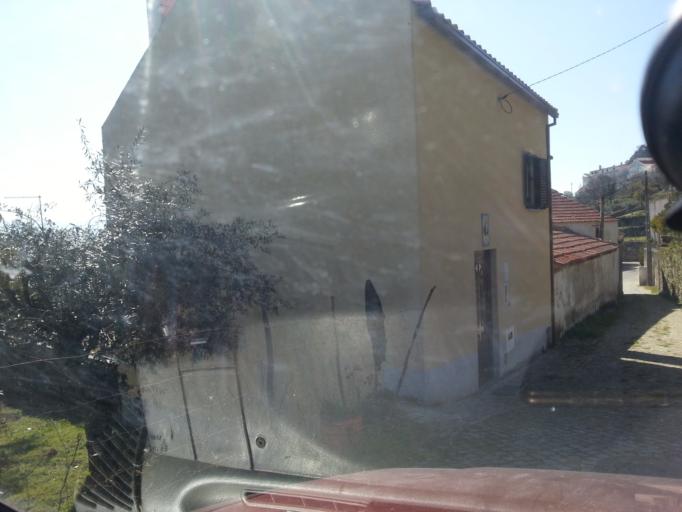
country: PT
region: Guarda
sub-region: Fornos de Algodres
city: Fornos de Algodres
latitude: 40.6243
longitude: -7.5379
